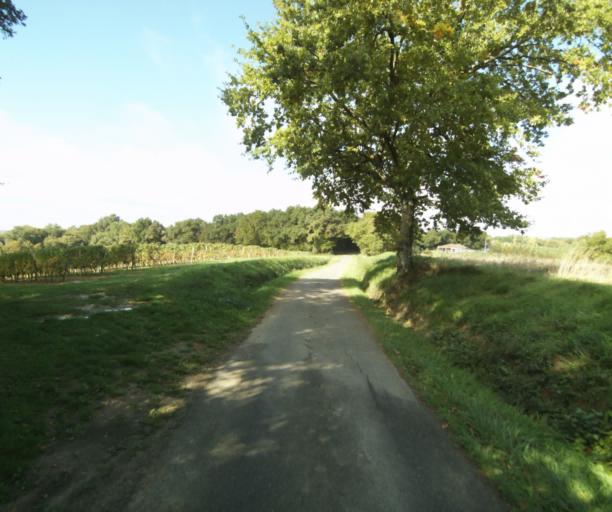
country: FR
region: Midi-Pyrenees
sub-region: Departement du Gers
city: Cazaubon
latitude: 43.8447
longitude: -0.0595
